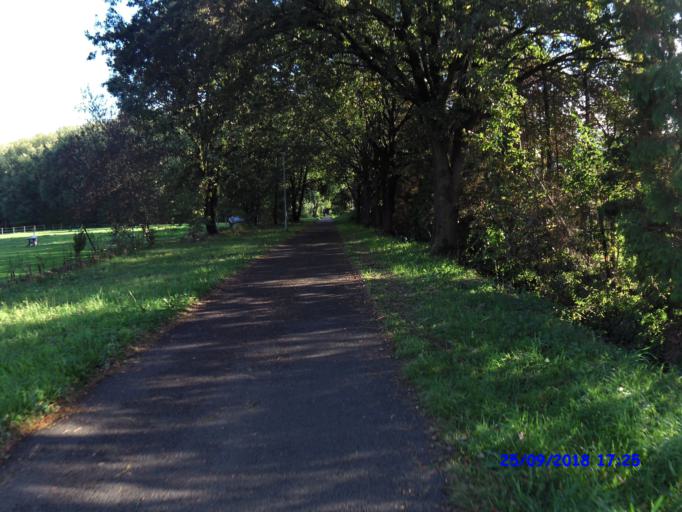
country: BE
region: Flanders
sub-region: Provincie Vlaams-Brabant
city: Aarschot
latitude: 51.0136
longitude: 4.8315
